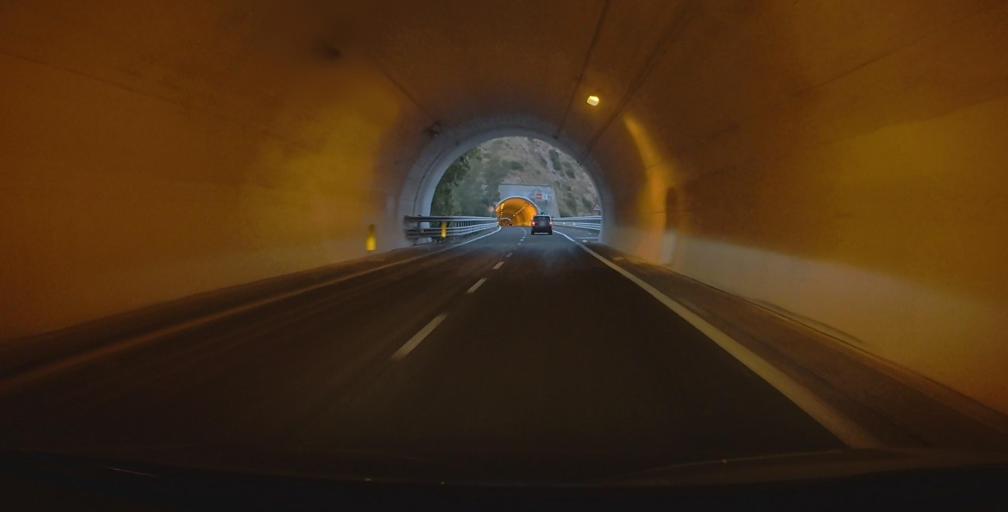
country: IT
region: Sicily
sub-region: Messina
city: Ali Terme
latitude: 38.0162
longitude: 15.4339
